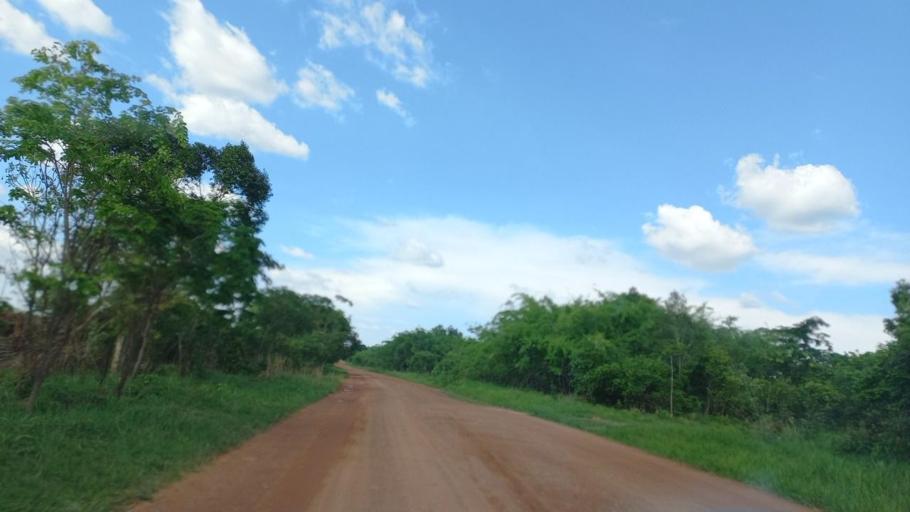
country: ZM
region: Copperbelt
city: Kitwe
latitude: -12.8522
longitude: 28.3902
